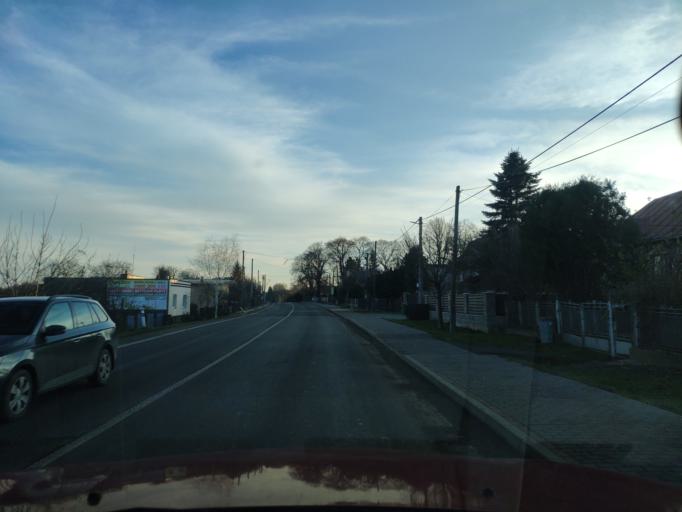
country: SK
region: Kosicky
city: Kosice
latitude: 48.8034
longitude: 21.3022
